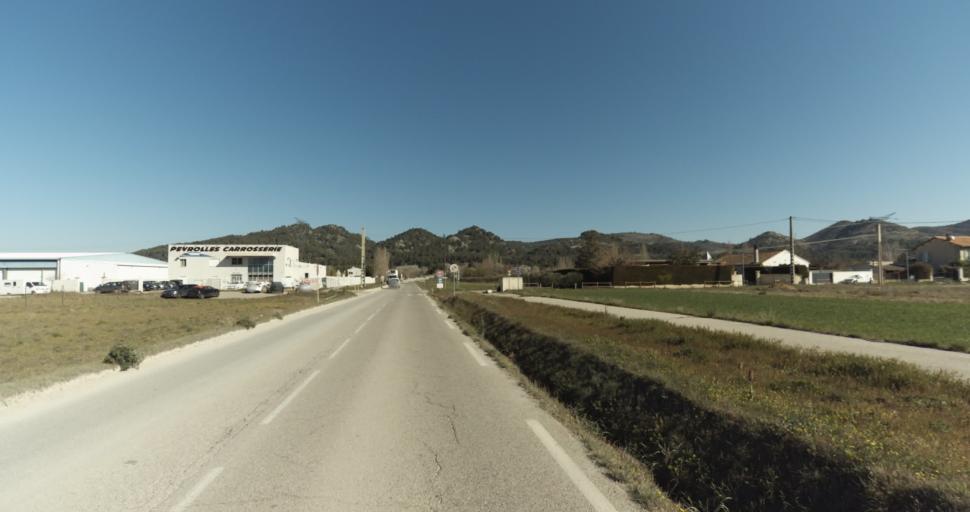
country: FR
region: Provence-Alpes-Cote d'Azur
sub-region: Departement des Bouches-du-Rhone
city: Peyrolles-en-Provence
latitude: 43.6544
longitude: 5.5802
